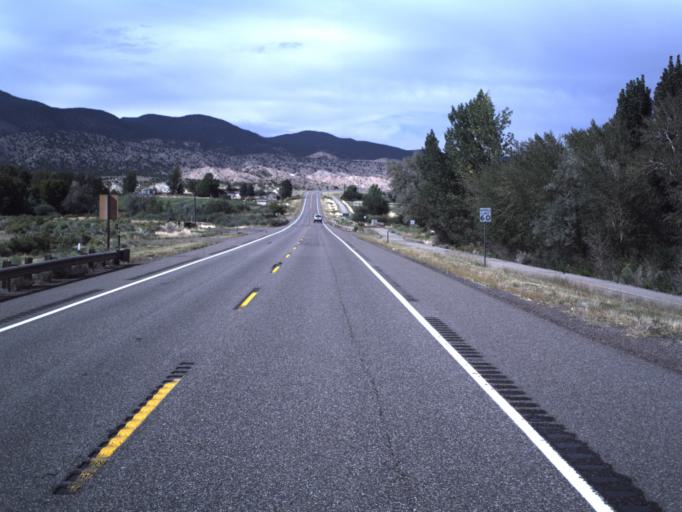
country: US
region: Utah
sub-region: Sevier County
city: Monroe
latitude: 38.5805
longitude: -112.2580
